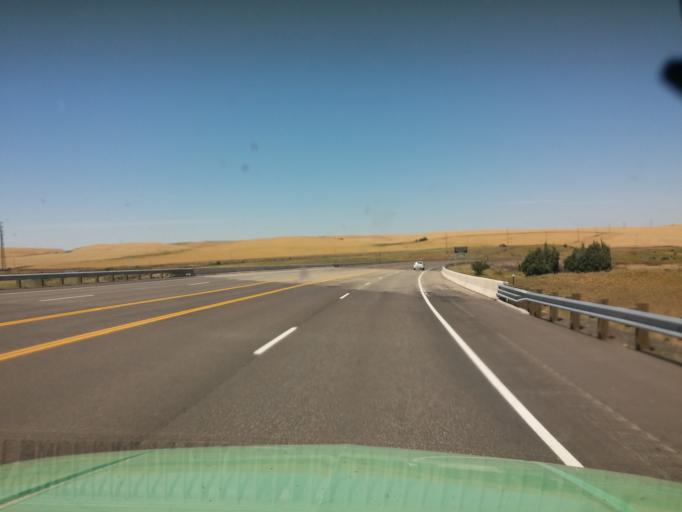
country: US
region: Washington
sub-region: Asotin County
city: Clarkston
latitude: 46.4732
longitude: -117.0361
